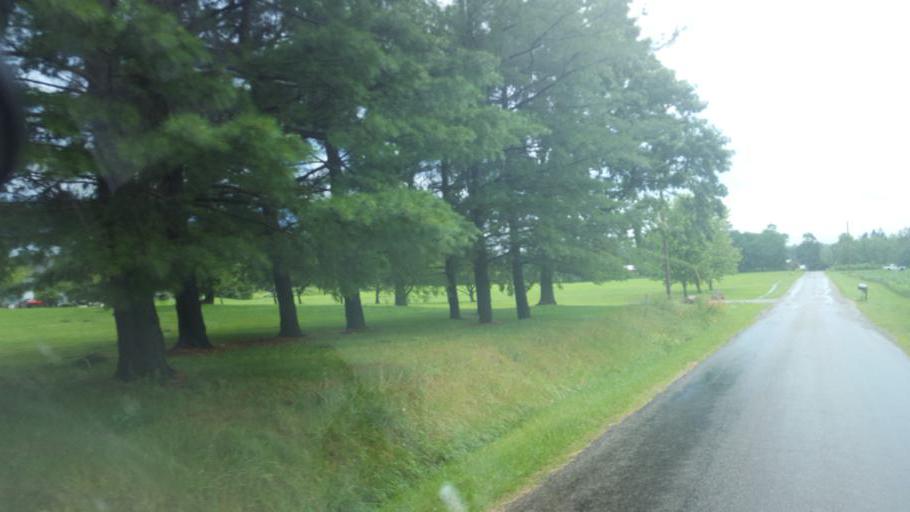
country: US
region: Ohio
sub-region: Richland County
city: Lexington
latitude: 40.6738
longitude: -82.6366
